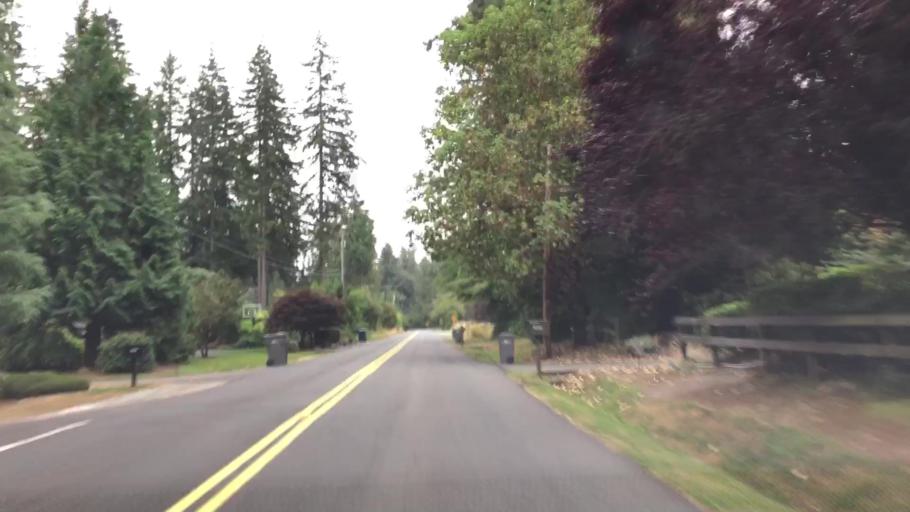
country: US
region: Washington
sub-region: King County
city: Woodinville
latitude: 47.7498
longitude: -122.1207
